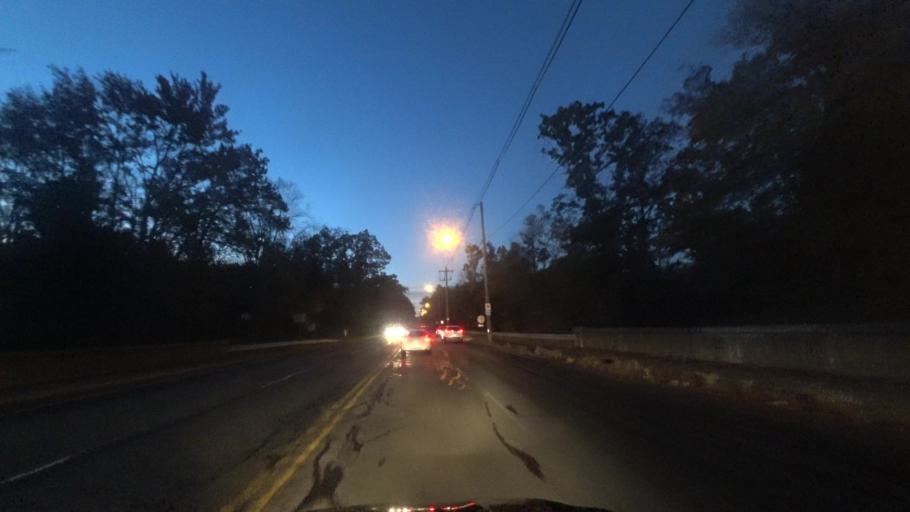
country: US
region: Massachusetts
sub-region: Middlesex County
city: North Reading
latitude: 42.5650
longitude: -71.1079
